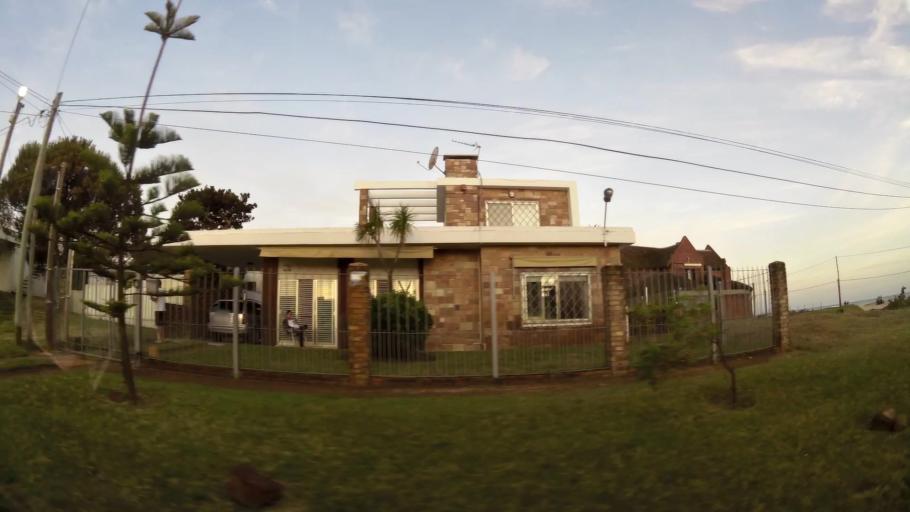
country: UY
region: Canelones
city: Atlantida
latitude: -34.7789
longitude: -55.7507
